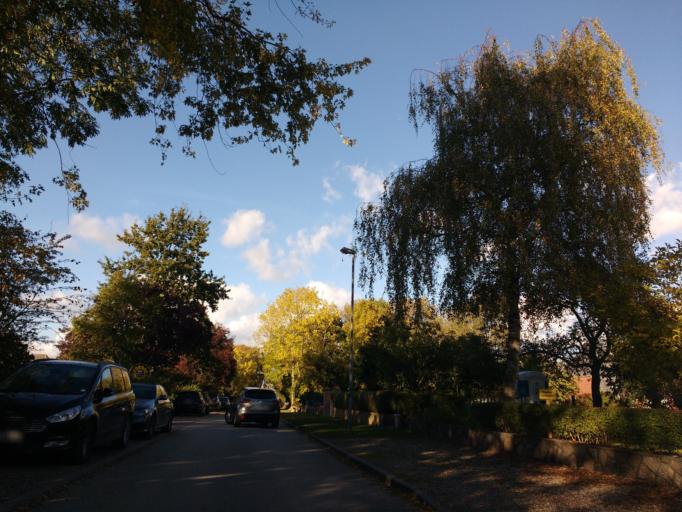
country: DE
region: Schleswig-Holstein
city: Grossenbrode
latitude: 54.4264
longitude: 11.1089
